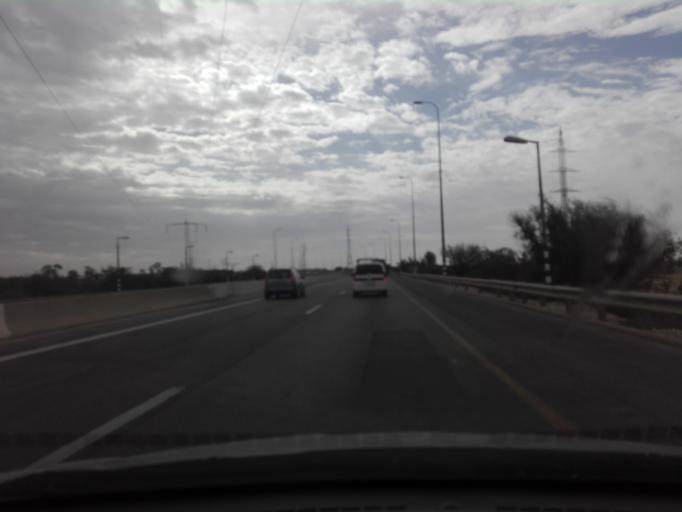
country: IL
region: Southern District
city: Lehavim
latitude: 31.3311
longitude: 34.7866
